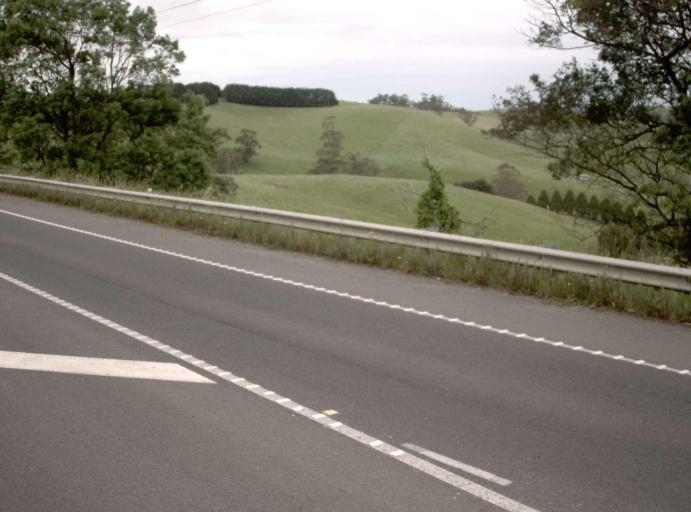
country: AU
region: Victoria
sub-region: Bass Coast
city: North Wonthaggi
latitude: -38.4163
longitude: 145.7811
